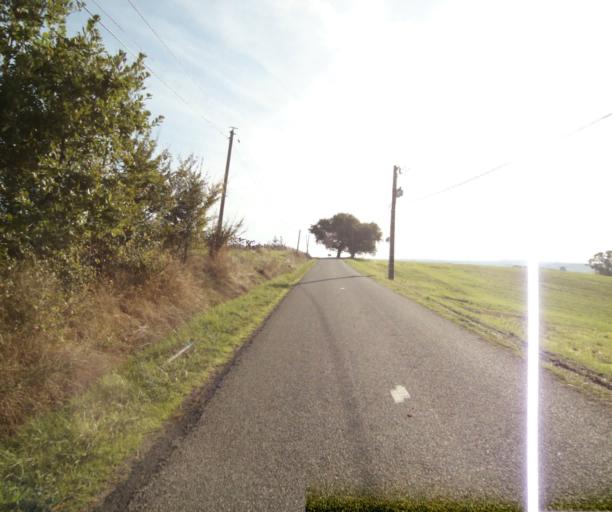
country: FR
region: Midi-Pyrenees
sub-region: Departement de la Haute-Garonne
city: Villemur-sur-Tarn
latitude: 43.9016
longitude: 1.4846
